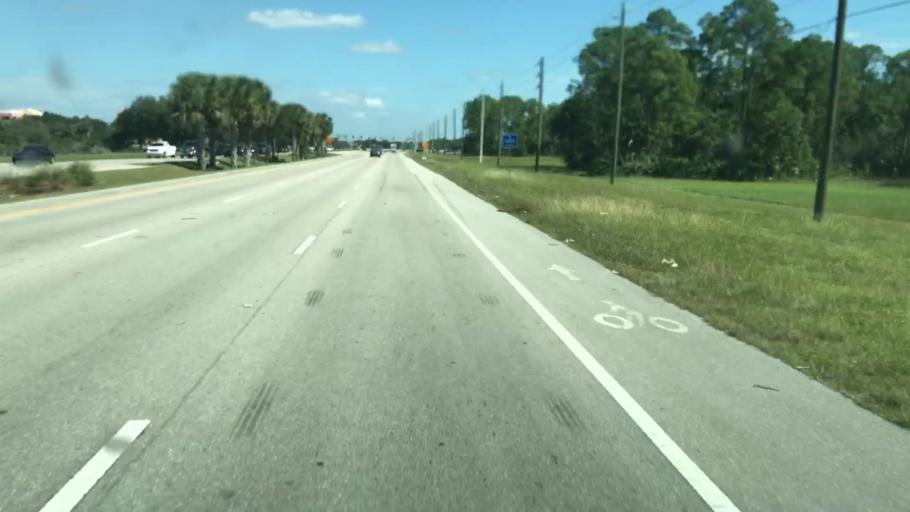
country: US
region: Florida
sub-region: Lee County
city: Gateway
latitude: 26.5538
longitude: -81.7539
